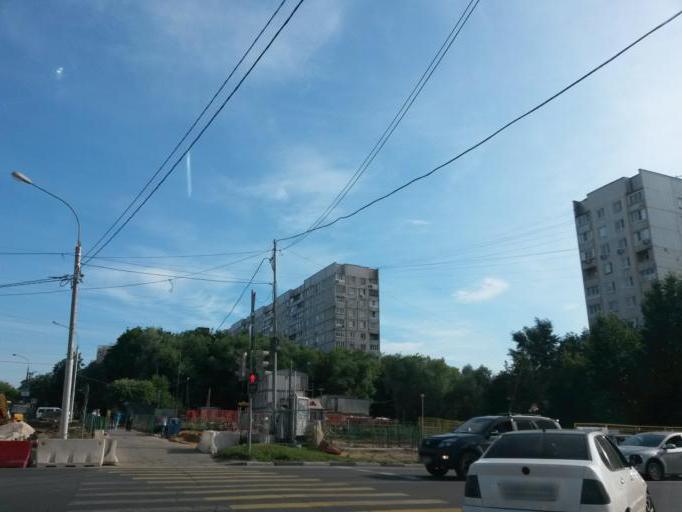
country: RU
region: Moscow
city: Orekhovo-Borisovo
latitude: 55.6269
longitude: 37.7420
